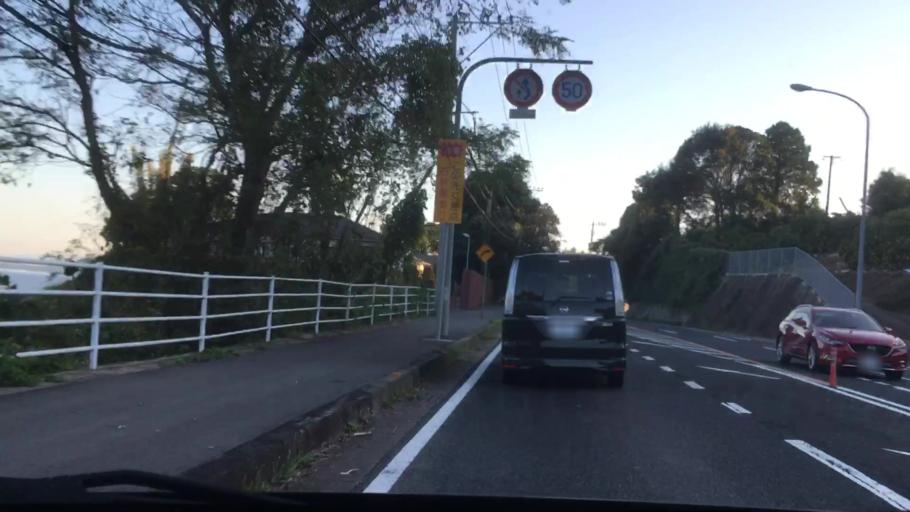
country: JP
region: Nagasaki
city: Sasebo
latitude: 33.0636
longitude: 129.7643
